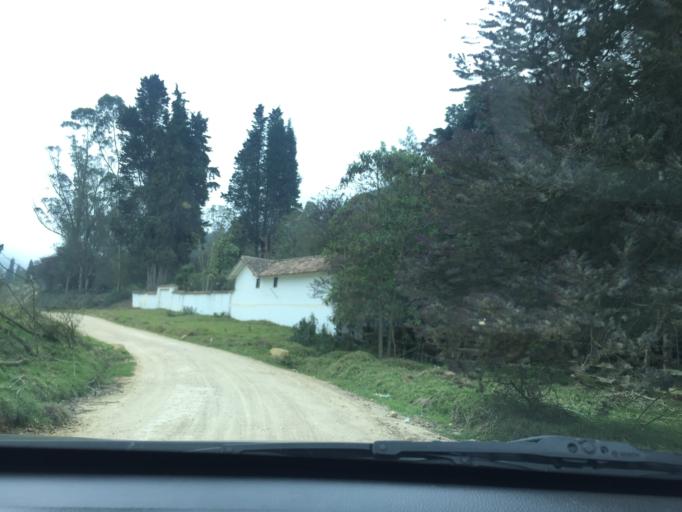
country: CO
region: Cundinamarca
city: Bojaca
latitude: 4.6840
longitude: -74.3190
